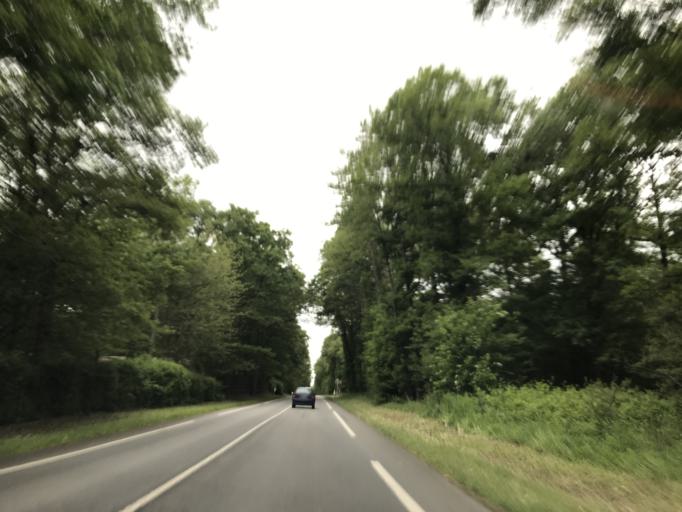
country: FR
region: Haute-Normandie
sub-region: Departement de l'Eure
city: La Couture-Boussey
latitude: 48.9052
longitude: 1.3843
